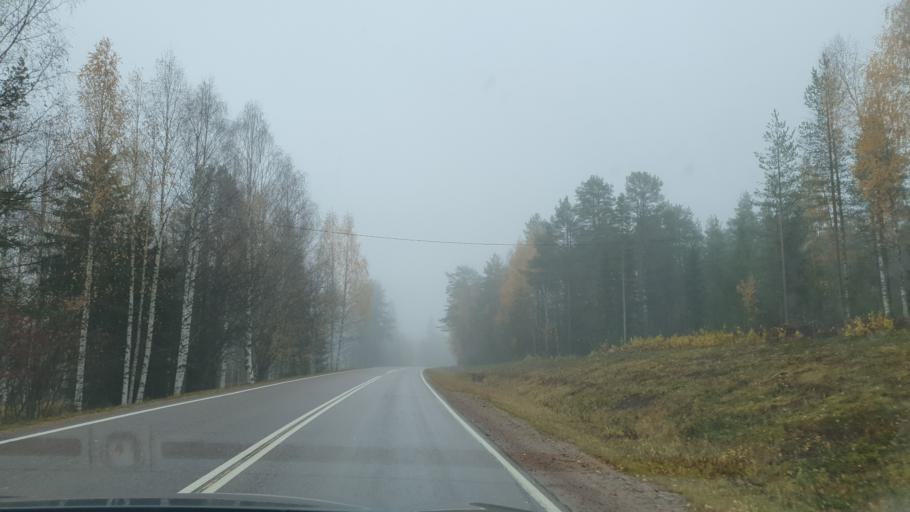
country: FI
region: Lapland
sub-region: Rovaniemi
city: Rovaniemi
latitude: 66.8112
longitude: 25.4056
